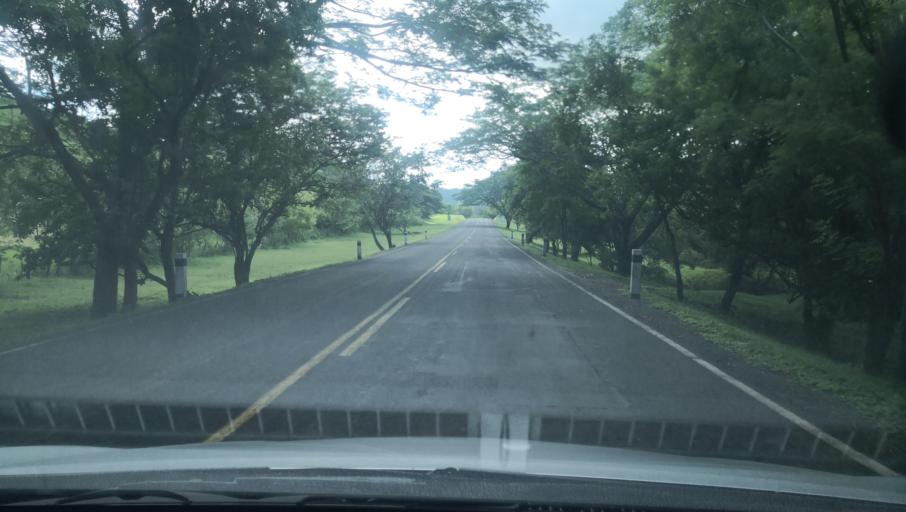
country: NI
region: Madriz
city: Somoto
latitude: 13.4654
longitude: -86.6449
